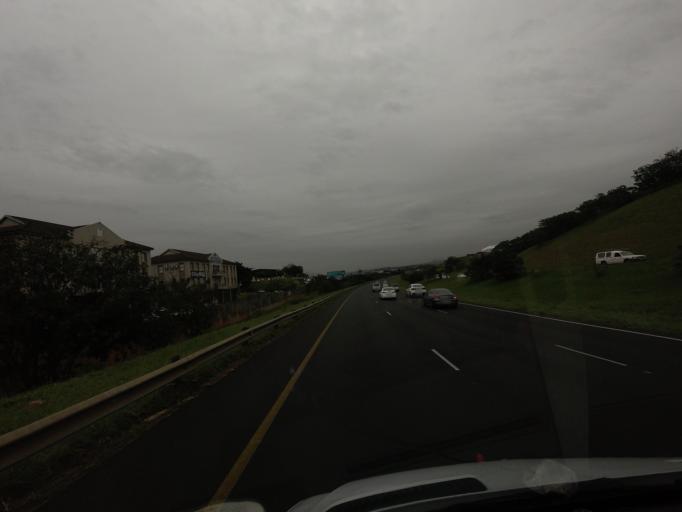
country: ZA
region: KwaZulu-Natal
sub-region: eThekwini Metropolitan Municipality
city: Durban
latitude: -29.7470
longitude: 31.0367
